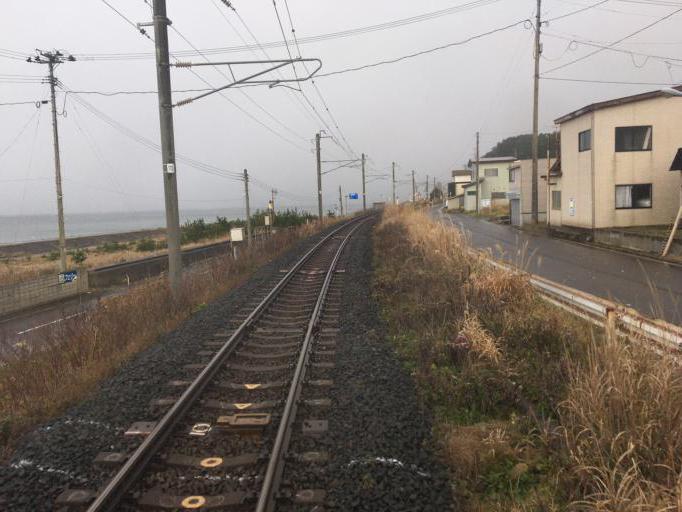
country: JP
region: Aomori
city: Aomori Shi
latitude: 41.0351
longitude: 140.6455
